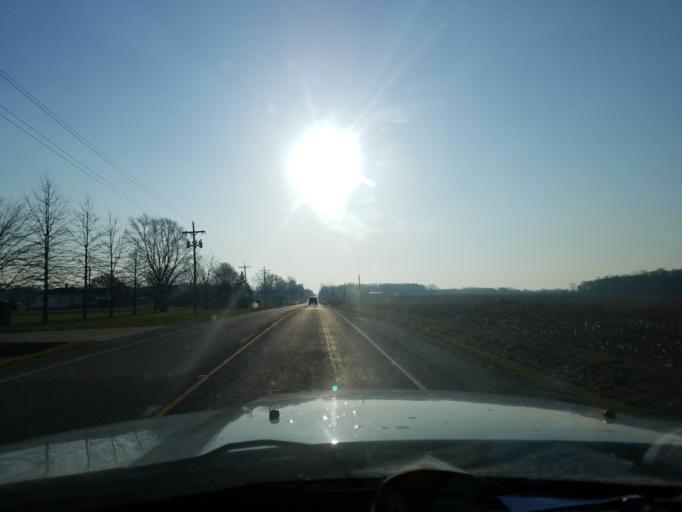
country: US
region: Indiana
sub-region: Vigo County
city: Seelyville
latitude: 39.3903
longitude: -87.2793
